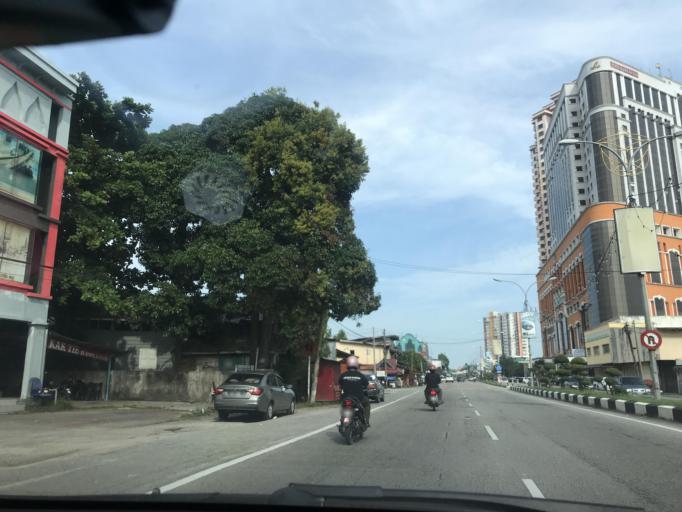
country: MY
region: Kelantan
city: Kota Bharu
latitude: 6.1149
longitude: 102.2486
